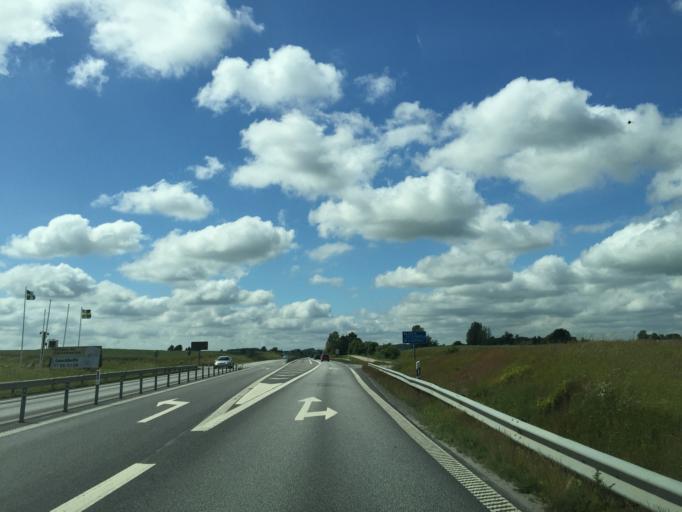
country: SE
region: Skane
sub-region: Skurups Kommun
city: Rydsgard
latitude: 55.4878
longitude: 13.5522
